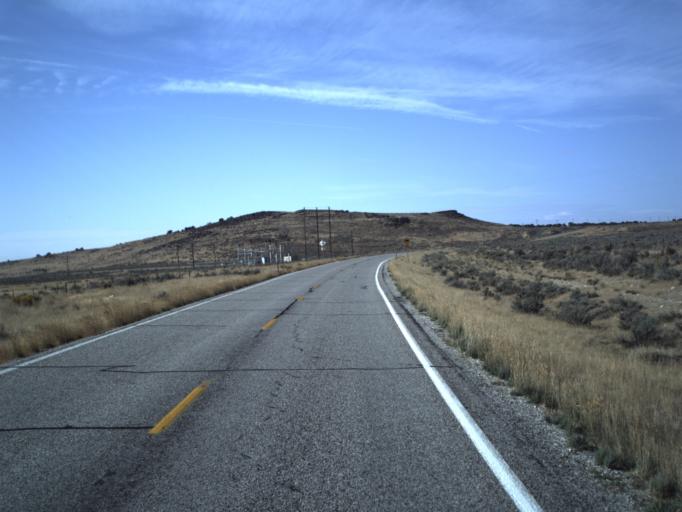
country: US
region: Idaho
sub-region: Minidoka County
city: Rupert
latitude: 41.8409
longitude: -113.1416
